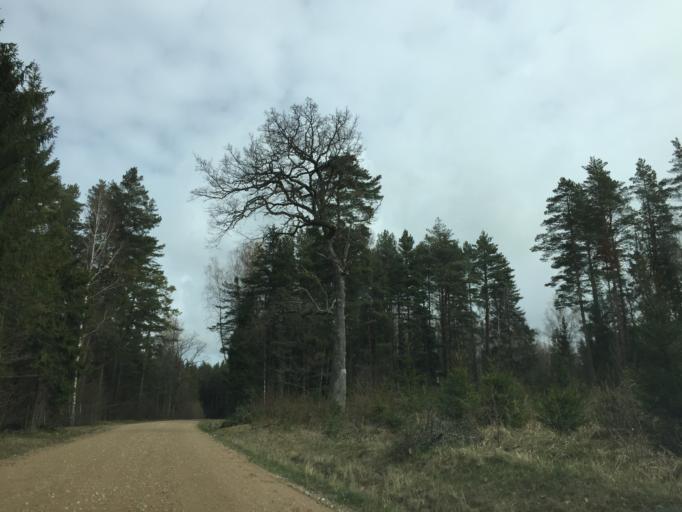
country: LV
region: Salacgrivas
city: Salacgriva
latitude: 57.5156
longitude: 24.4141
